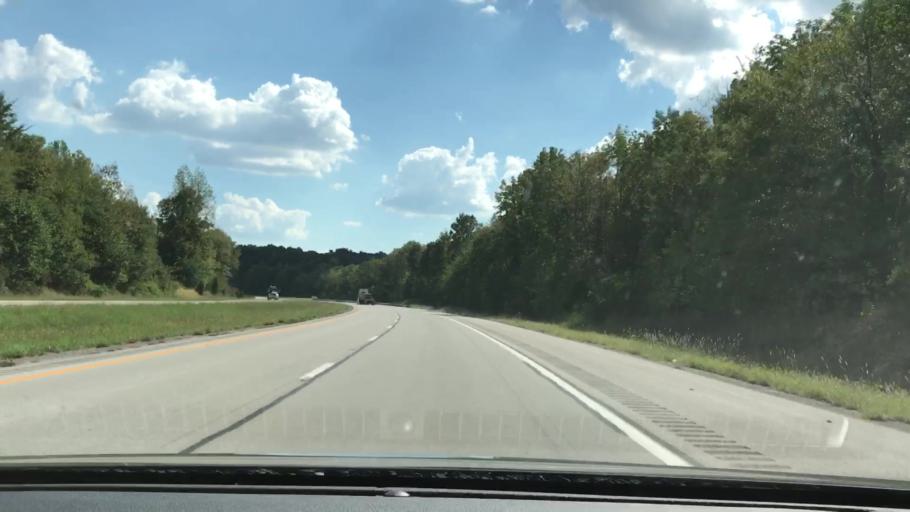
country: US
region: Kentucky
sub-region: Butler County
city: Morgantown
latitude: 37.2655
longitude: -86.7485
